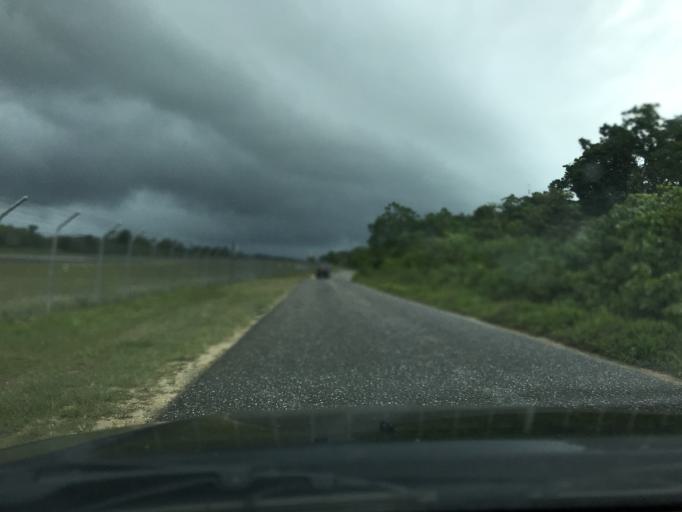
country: SB
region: Western Province
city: Gizo
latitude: -8.3246
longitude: 157.2711
